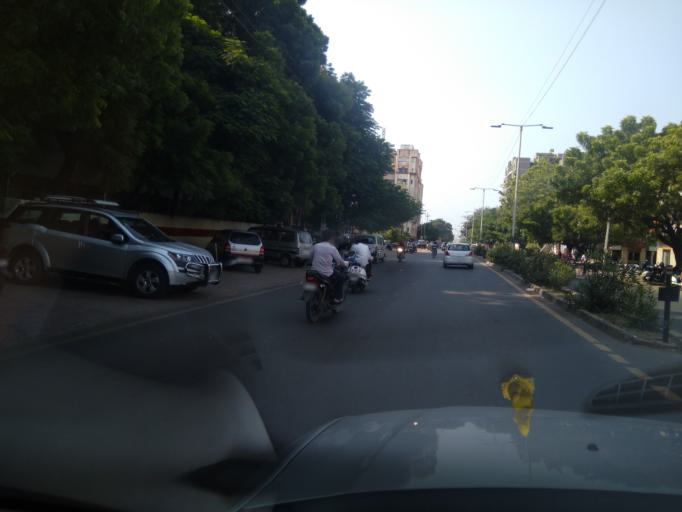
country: IN
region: Gujarat
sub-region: Jamnagar
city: Jamnagar
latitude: 22.4634
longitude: 70.0511
